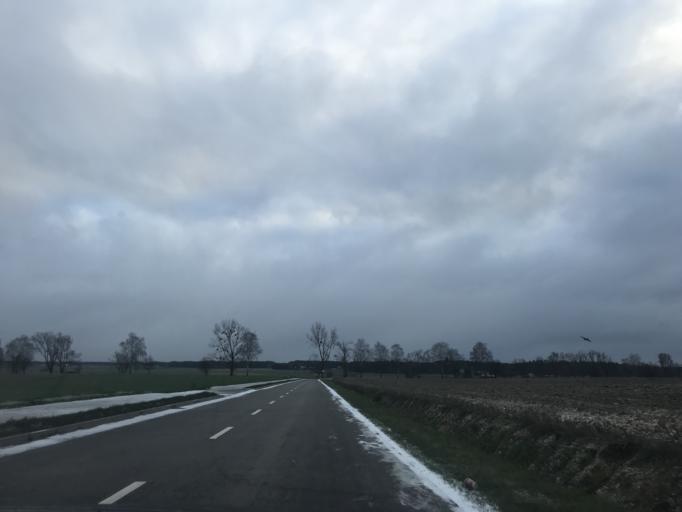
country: PL
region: Pomeranian Voivodeship
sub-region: Powiat chojnicki
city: Brusy
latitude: 53.8705
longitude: 17.7543
